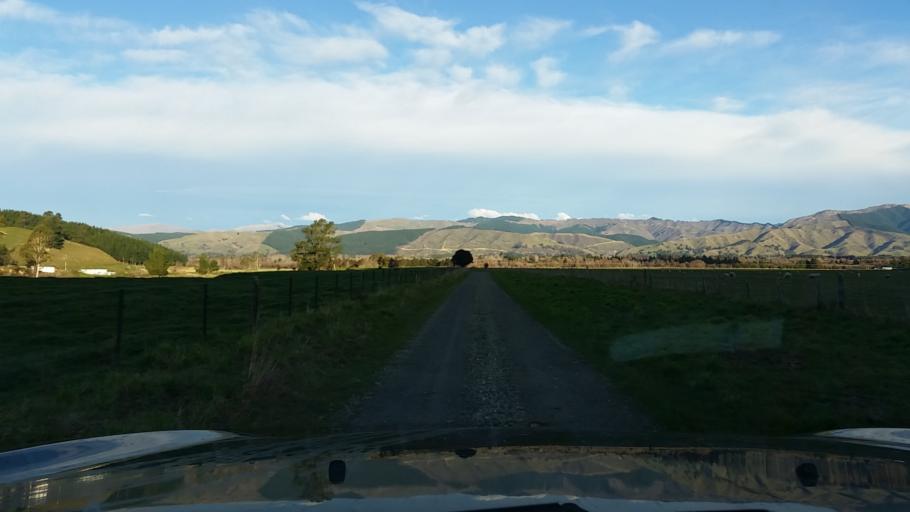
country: NZ
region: Nelson
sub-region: Nelson City
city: Nelson
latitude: -41.5343
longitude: 173.4881
